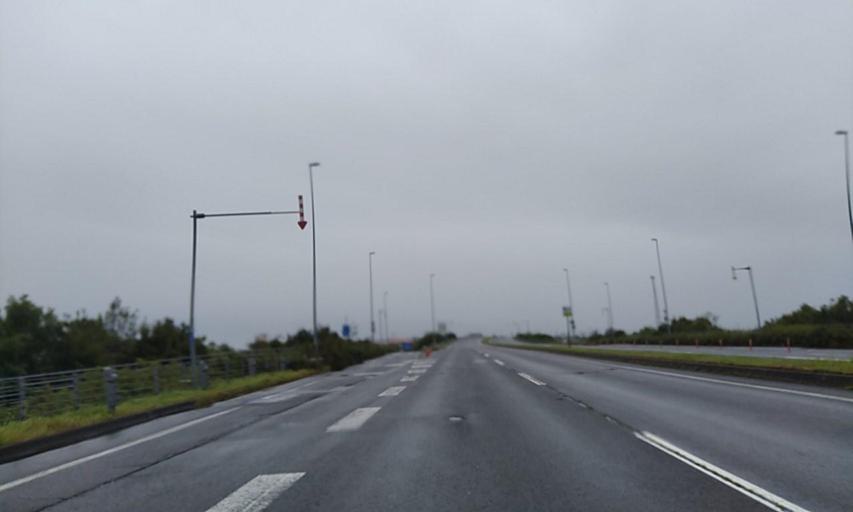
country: JP
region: Hokkaido
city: Kushiro
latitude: 43.0126
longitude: 144.2567
